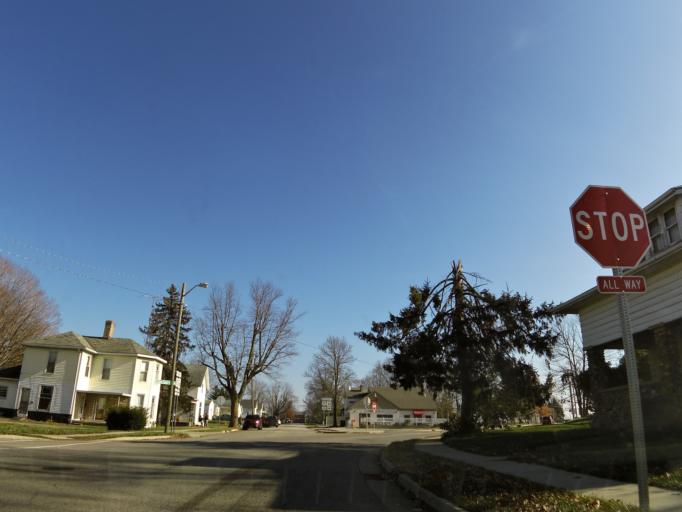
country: US
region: Indiana
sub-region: Union County
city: Liberty
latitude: 39.6346
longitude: -84.9258
